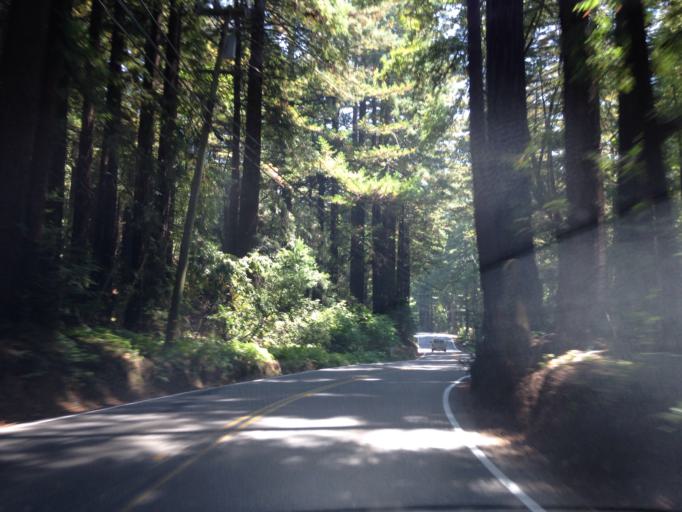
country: US
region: California
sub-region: Marin County
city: Lagunitas-Forest Knolls
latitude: 38.0496
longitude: -122.6764
